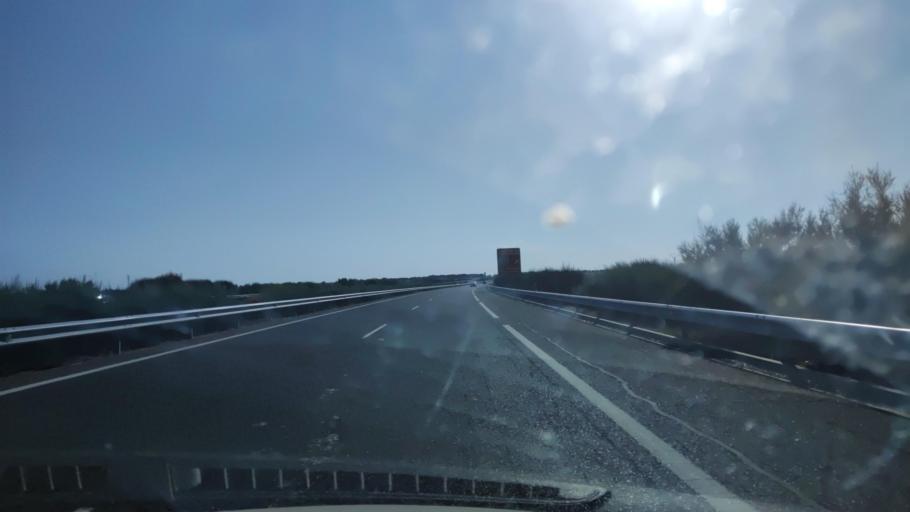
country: ES
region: Castille and Leon
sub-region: Provincia de Salamanca
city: La Fuente de San Esteban
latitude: 40.7930
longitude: -6.2188
